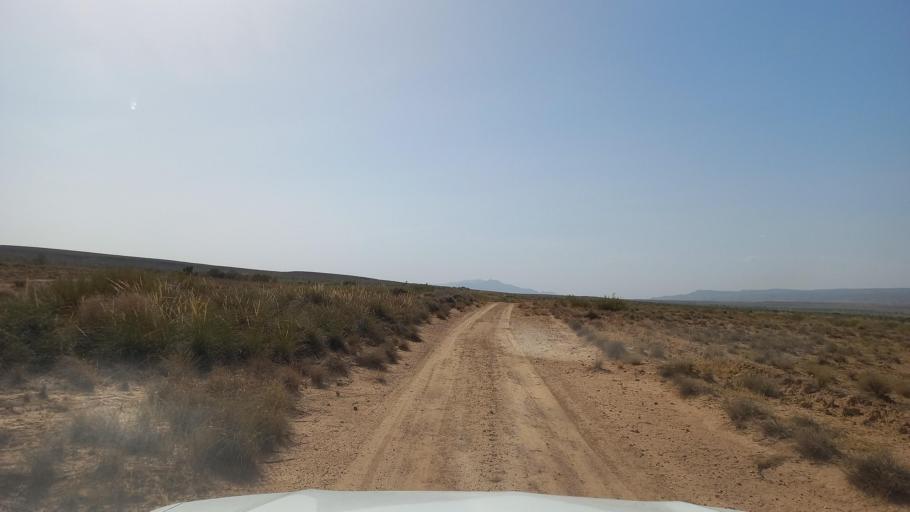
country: TN
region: Al Qasrayn
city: Kasserine
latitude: 35.2144
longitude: 9.0091
